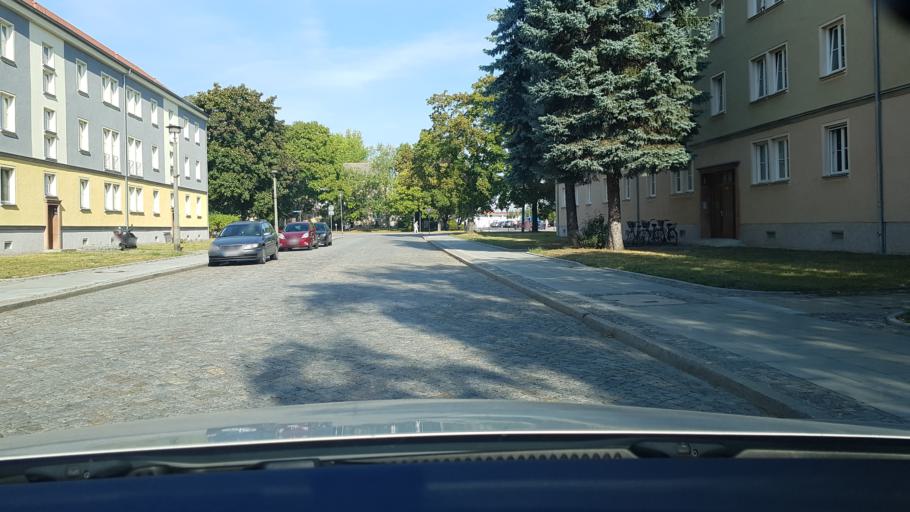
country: DE
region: Brandenburg
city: Eisenhuettenstadt
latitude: 52.1475
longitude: 14.6227
